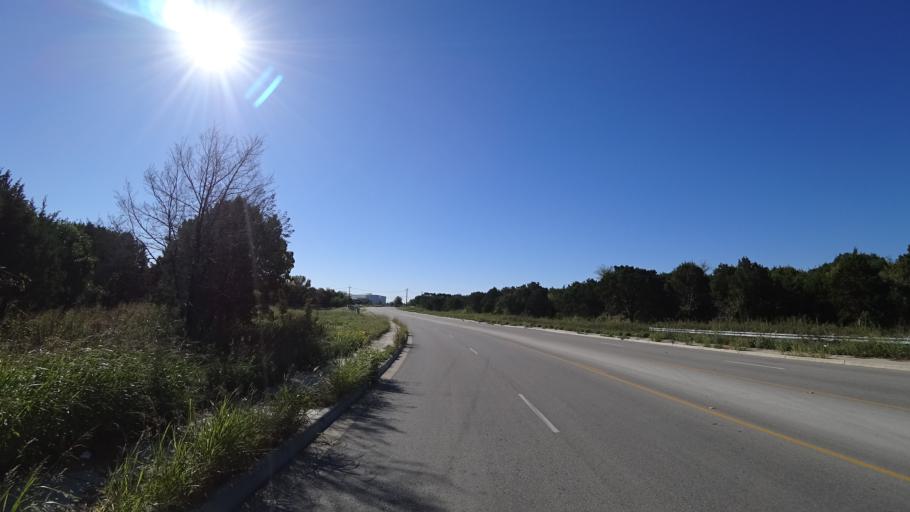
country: US
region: Texas
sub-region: Travis County
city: Austin
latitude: 30.3258
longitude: -97.6594
